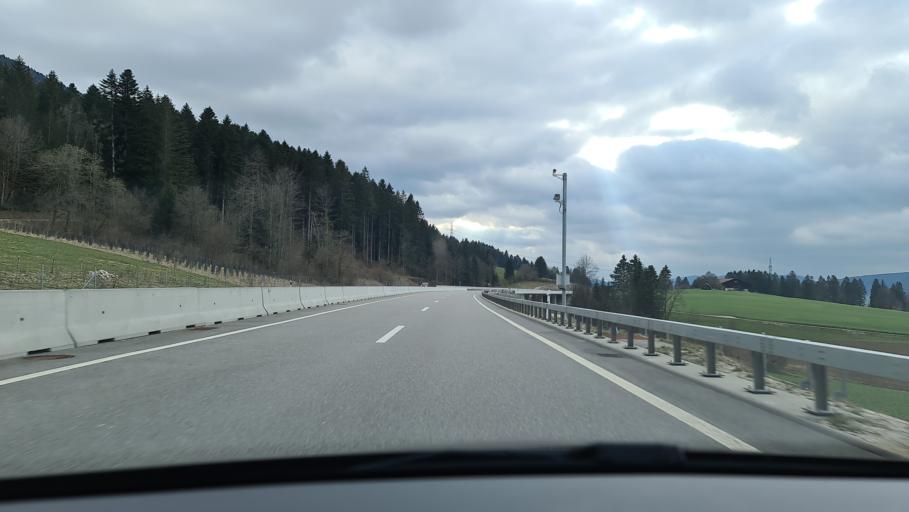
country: CH
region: Bern
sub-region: Jura bernois
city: Bevilard
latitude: 47.2326
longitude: 7.3087
